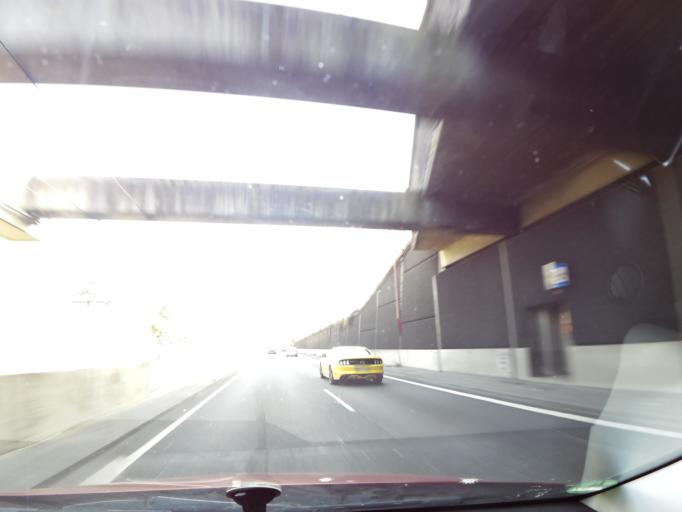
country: DE
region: North Rhine-Westphalia
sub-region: Regierungsbezirk Koln
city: Konigswinter
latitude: 50.6916
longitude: 7.1871
